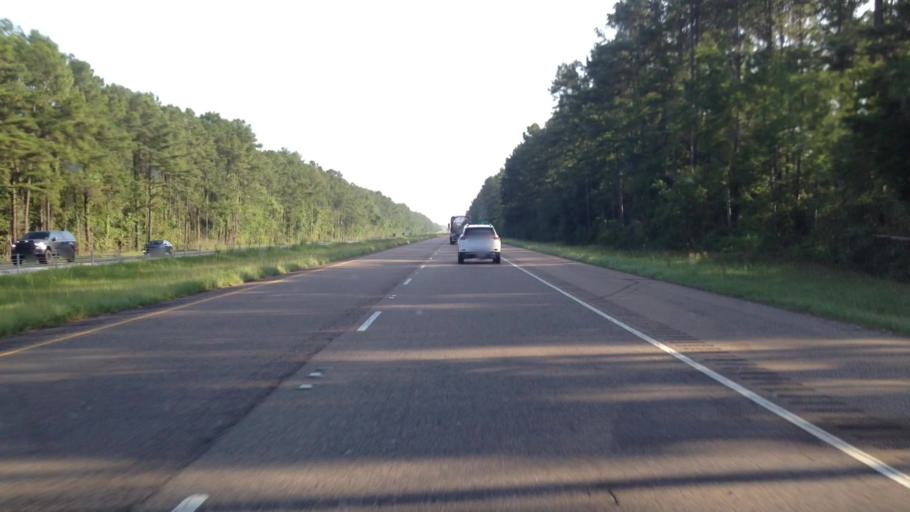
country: US
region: Louisiana
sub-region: Tangipahoa Parish
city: Amite
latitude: 30.7052
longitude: -90.5326
